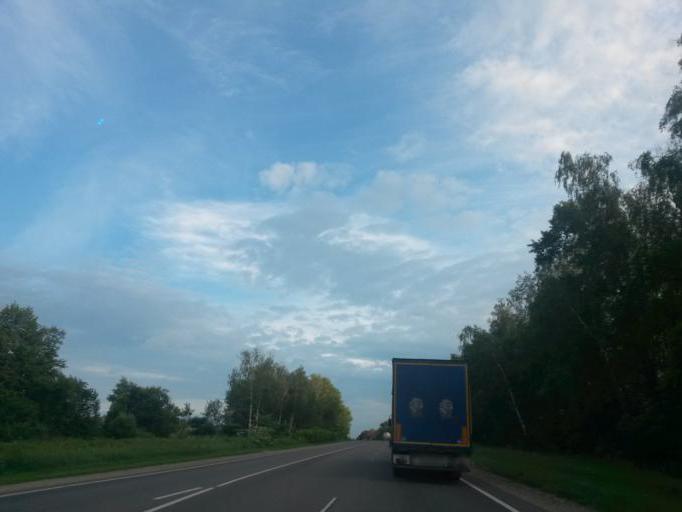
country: RU
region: Moskovskaya
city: Barybino
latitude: 55.2205
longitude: 37.8672
